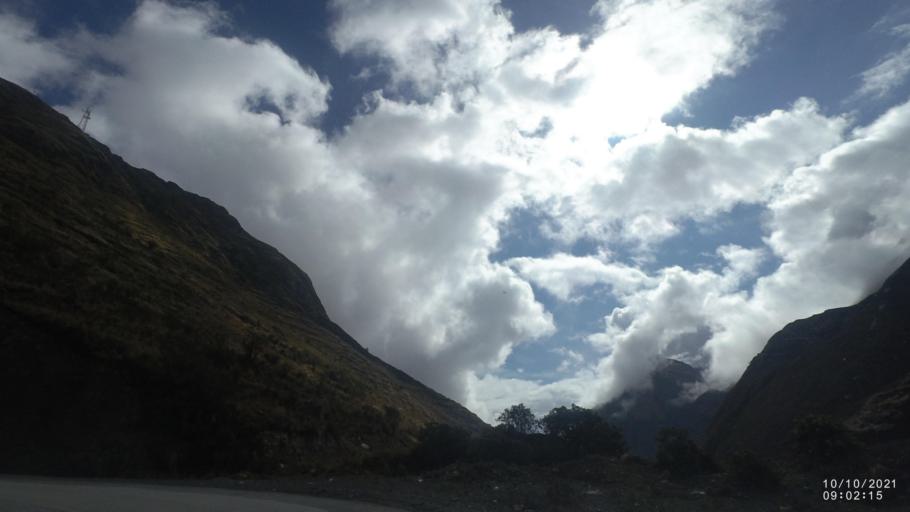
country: BO
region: La Paz
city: Quime
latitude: -17.0017
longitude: -67.2674
